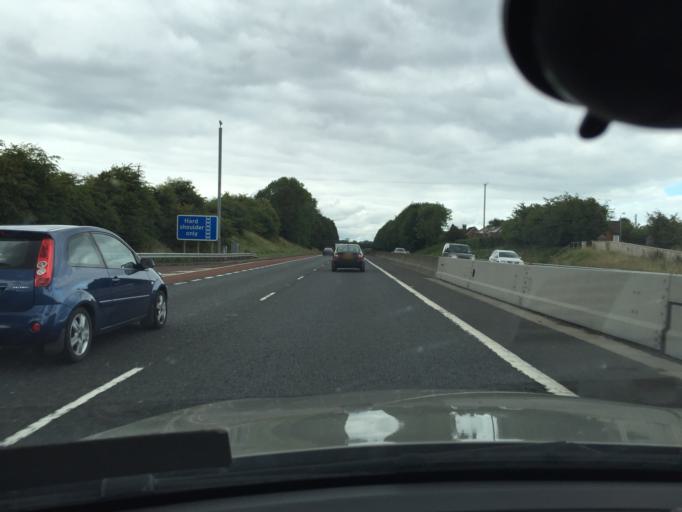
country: GB
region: Northern Ireland
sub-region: Lisburn District
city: Lisburn
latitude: 54.5305
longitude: -6.0003
